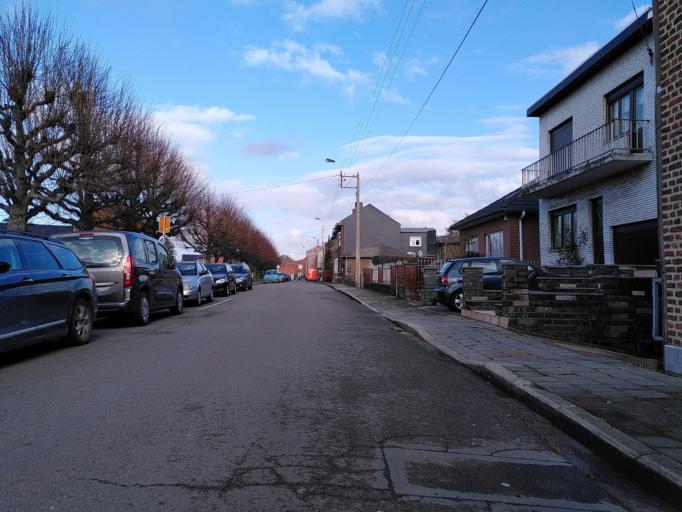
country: BE
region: Wallonia
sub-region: Province de Liege
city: Herstal
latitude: 50.6616
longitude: 5.6520
